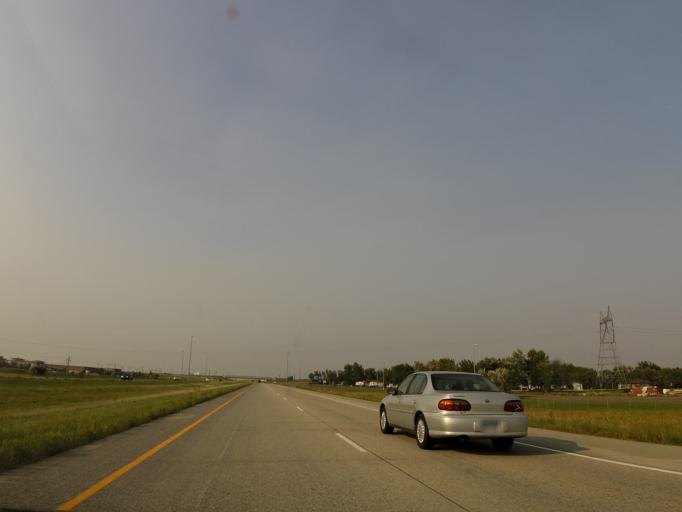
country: US
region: North Dakota
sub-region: Cass County
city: Horace
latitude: 46.7952
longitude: -96.8387
